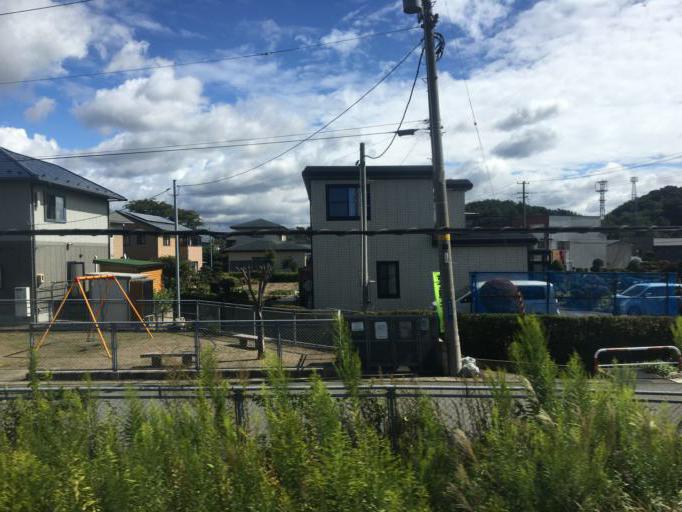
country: JP
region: Akita
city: Akita
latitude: 39.7069
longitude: 140.1281
